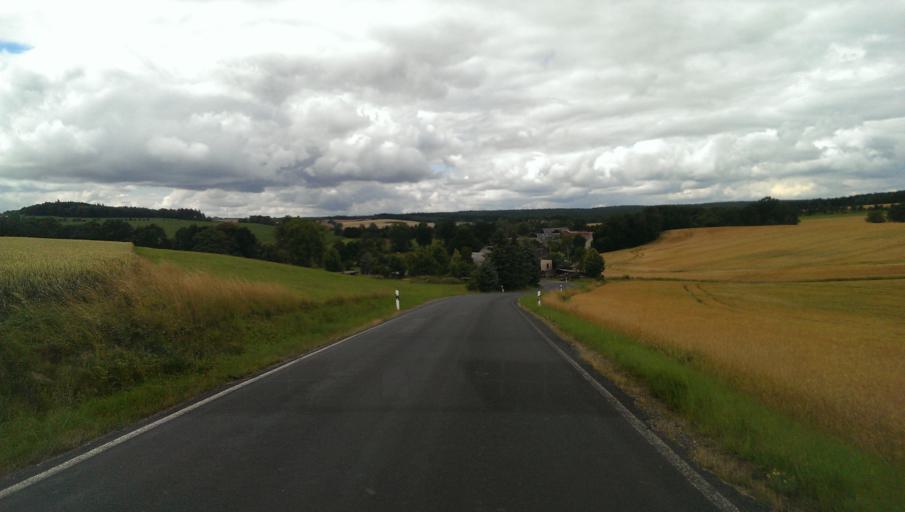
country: DE
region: Saxony
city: Pausa
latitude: 50.5984
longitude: 11.9914
